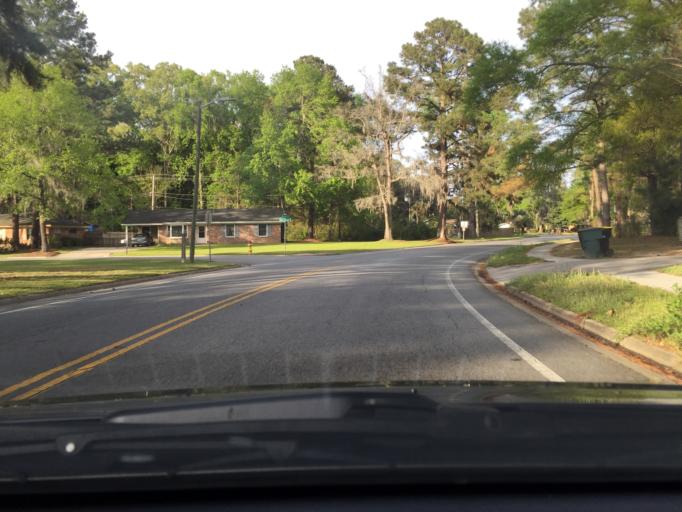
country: US
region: Georgia
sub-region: Chatham County
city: Montgomery
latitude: 31.9859
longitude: -81.1472
